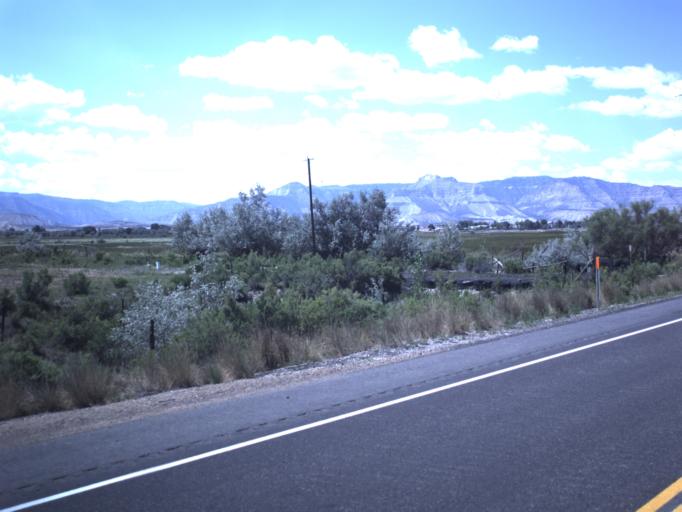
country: US
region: Utah
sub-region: Emery County
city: Huntington
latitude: 39.3076
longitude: -110.9642
